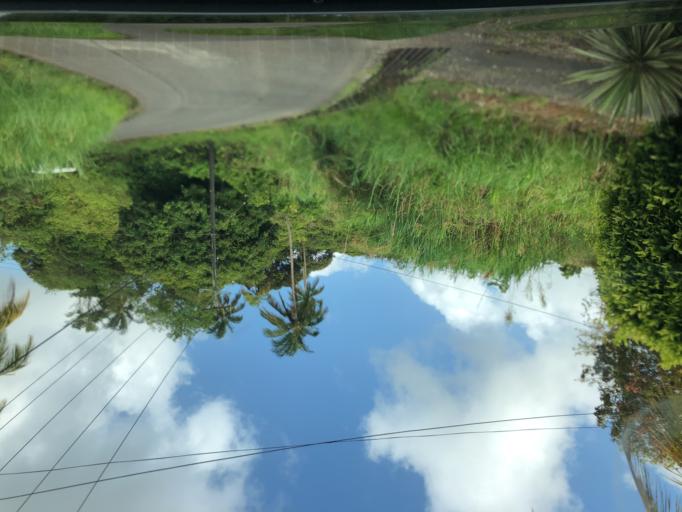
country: LC
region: Castries Quarter
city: Bisee
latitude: 13.9922
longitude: -60.9563
